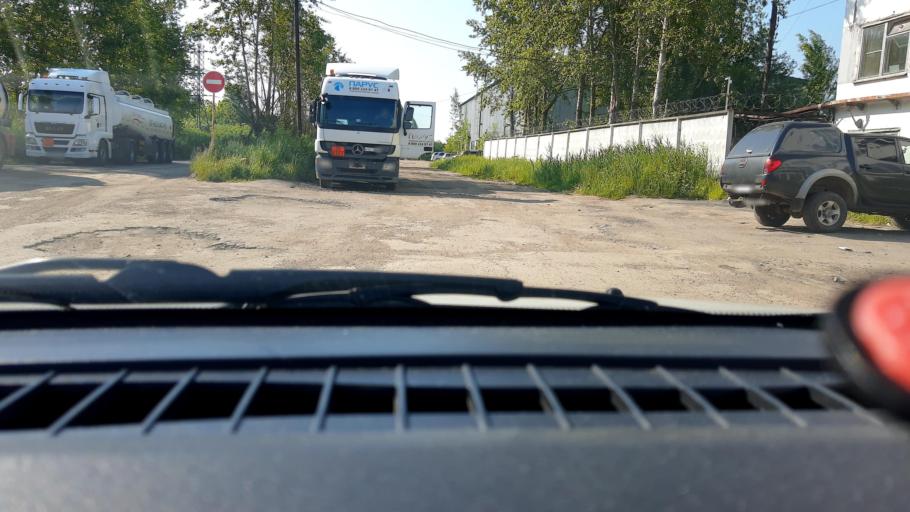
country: RU
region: Nizjnij Novgorod
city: Burevestnik
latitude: 56.1733
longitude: 43.9100
